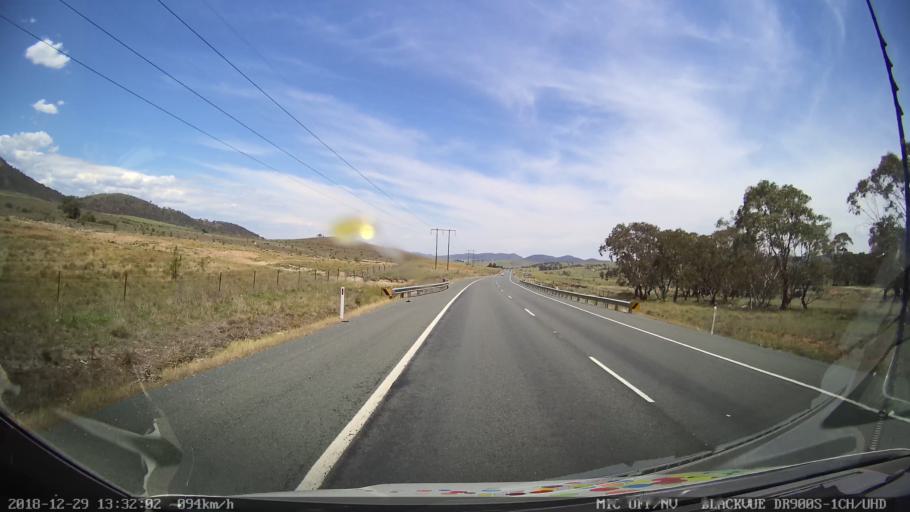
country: AU
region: New South Wales
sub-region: Cooma-Monaro
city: Cooma
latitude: -35.9249
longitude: 149.1515
